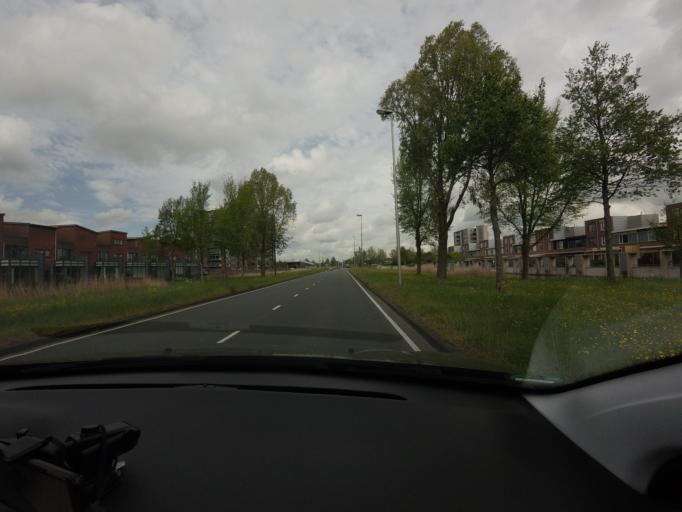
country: NL
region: North Holland
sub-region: Gemeente Purmerend
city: Purmerend
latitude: 52.4936
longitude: 4.9409
